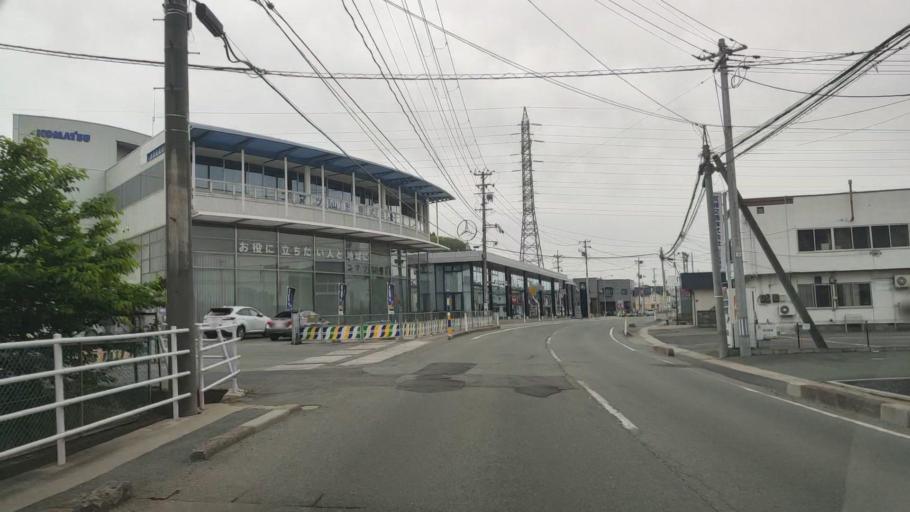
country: JP
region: Yamagata
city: Yamagata-shi
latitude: 38.2098
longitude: 140.3224
